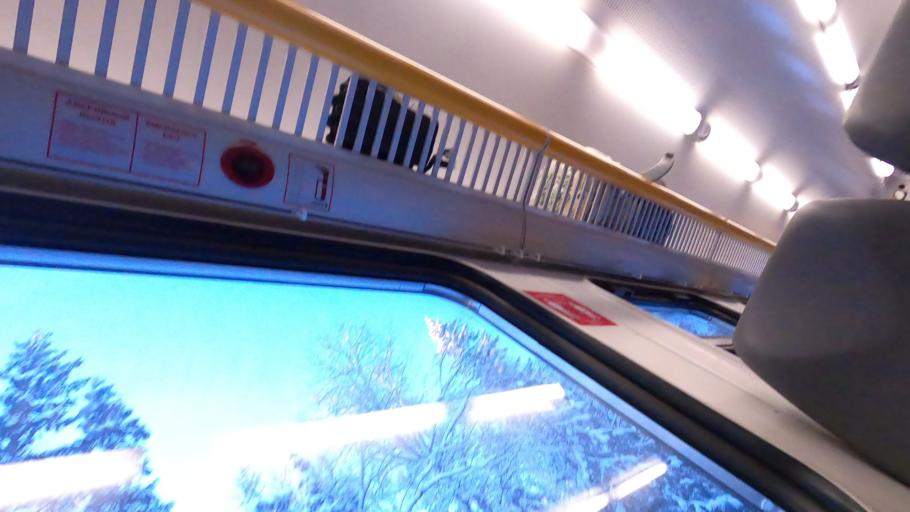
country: RU
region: Moskovskaya
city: Novo-Nikol'skoye
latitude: 56.6308
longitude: 37.5633
